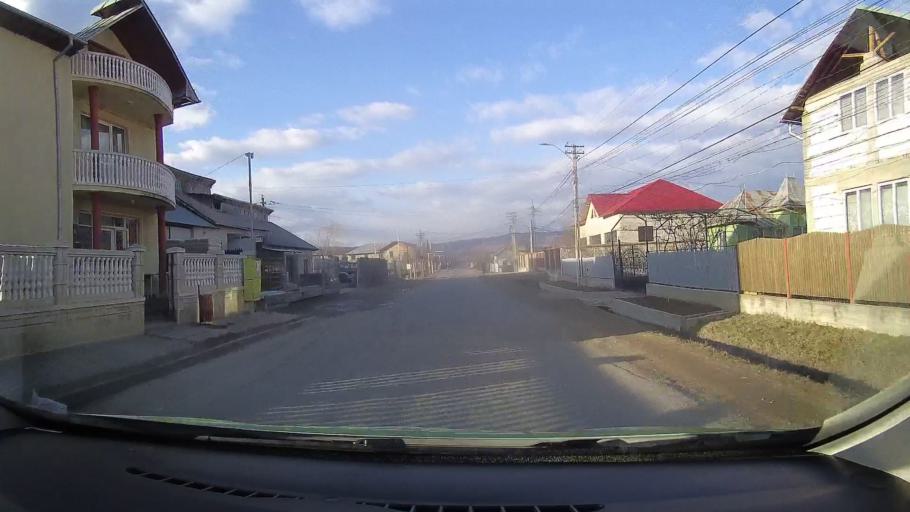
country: RO
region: Dambovita
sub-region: Comuna Ocnita
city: Ocnita
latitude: 44.9752
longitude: 25.5561
